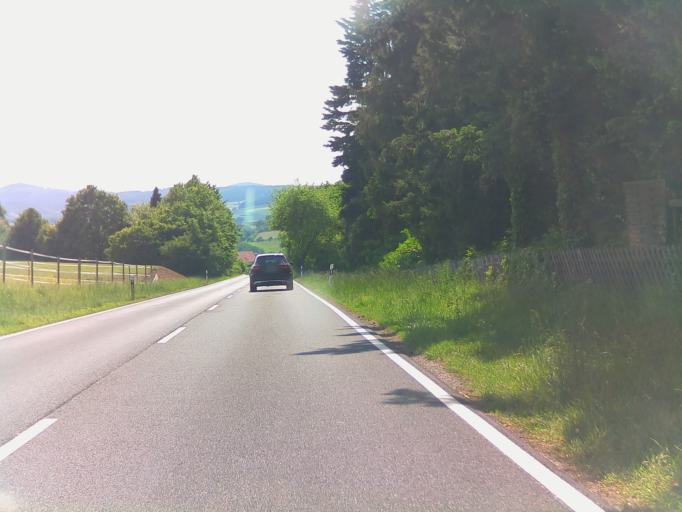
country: DE
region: Hesse
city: Tann
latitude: 50.6393
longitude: 10.0281
